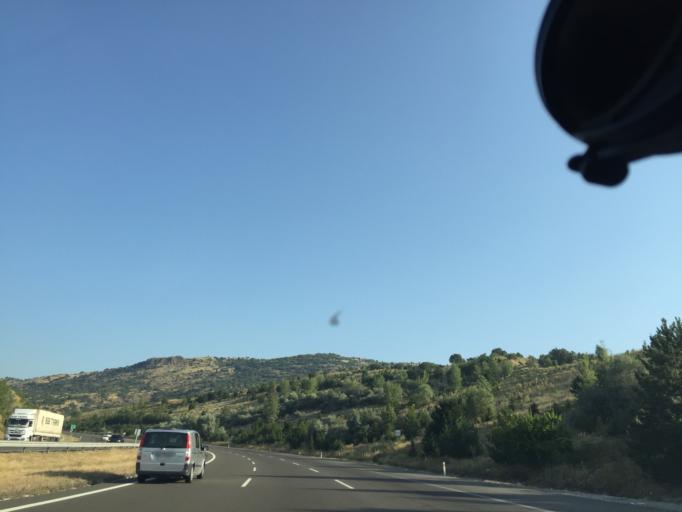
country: TR
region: Ankara
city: Celtikci
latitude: 40.3766
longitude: 32.4710
